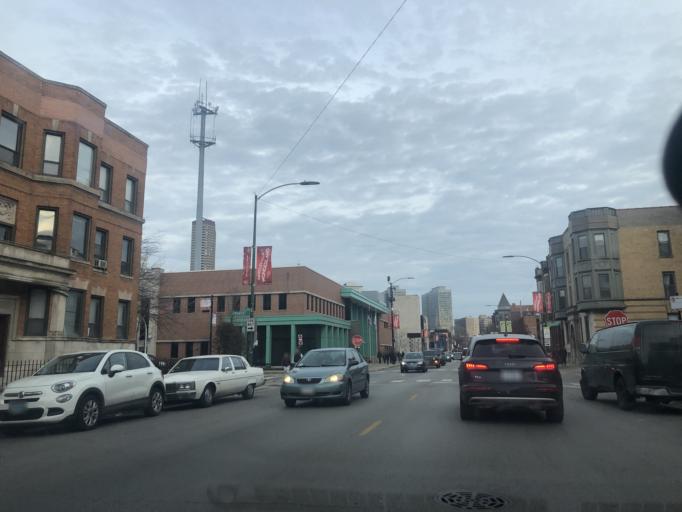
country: US
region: Illinois
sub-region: Cook County
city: Lincolnwood
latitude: 41.9472
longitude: -87.6524
